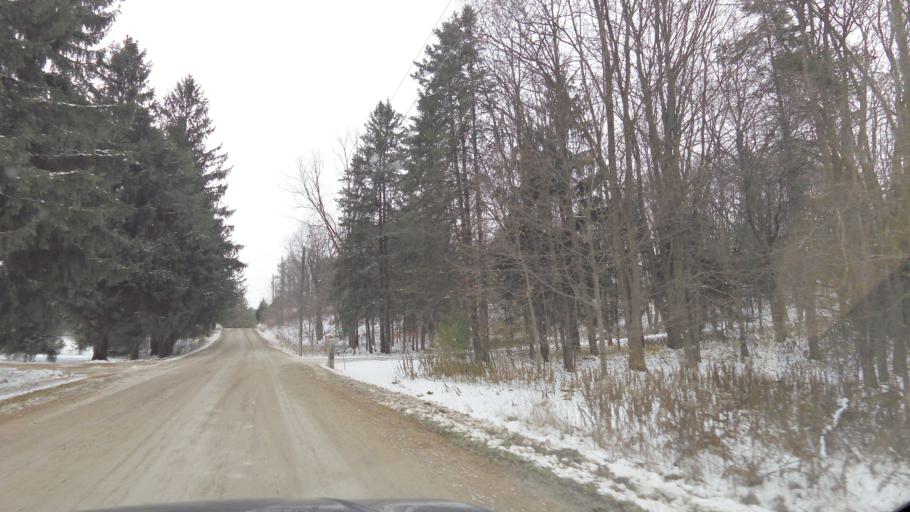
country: CA
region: Ontario
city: Vaughan
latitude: 43.9459
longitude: -79.6115
